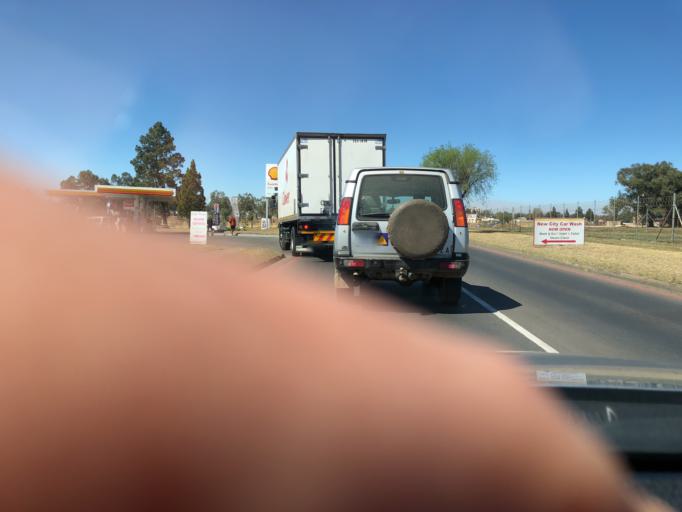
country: ZA
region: KwaZulu-Natal
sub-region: Amajuba District Municipality
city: Newcastle
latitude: -27.7598
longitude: 29.9451
